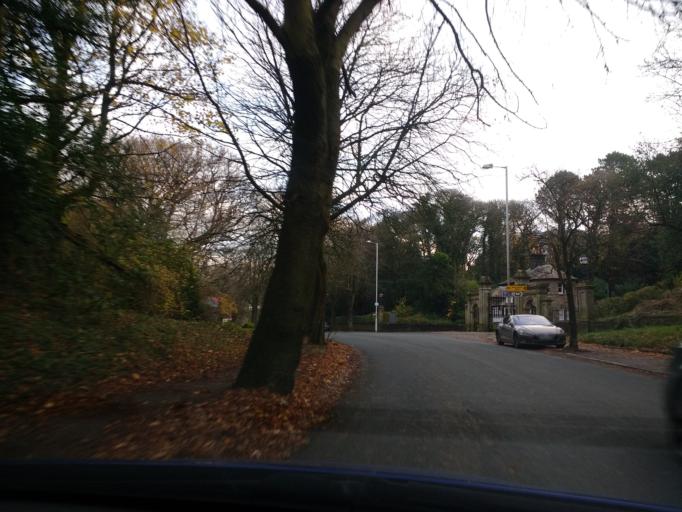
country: GB
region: England
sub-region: Lancashire
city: Lancaster
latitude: 54.0477
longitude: -2.7822
